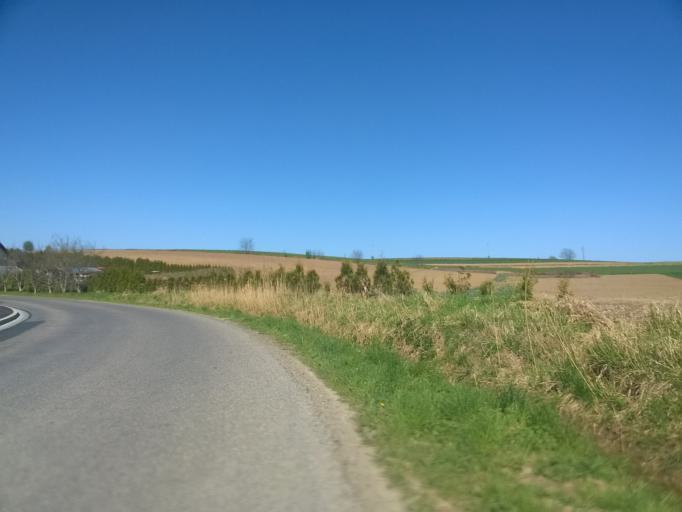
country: PL
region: Lesser Poland Voivodeship
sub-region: Powiat krakowski
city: Michalowice
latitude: 50.1164
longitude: 19.9971
